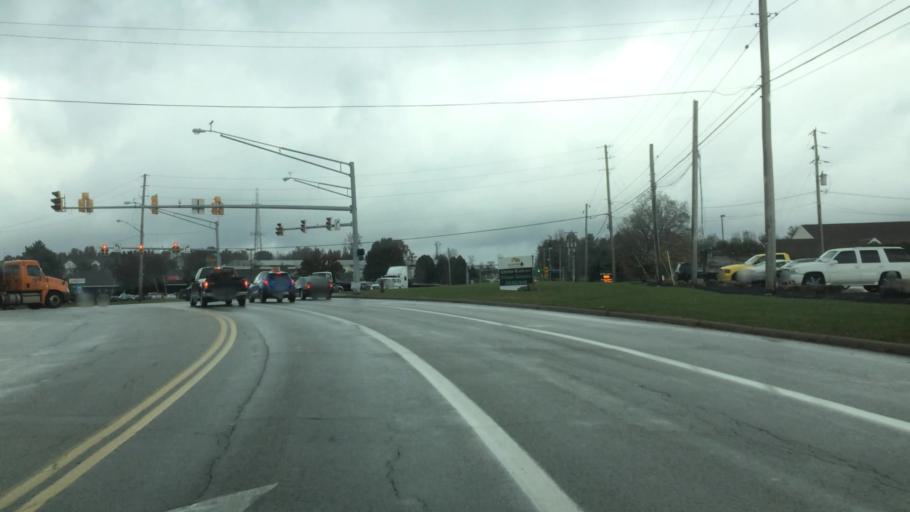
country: US
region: Ohio
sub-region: Summit County
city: Silver Lake
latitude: 41.1809
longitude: -81.4735
